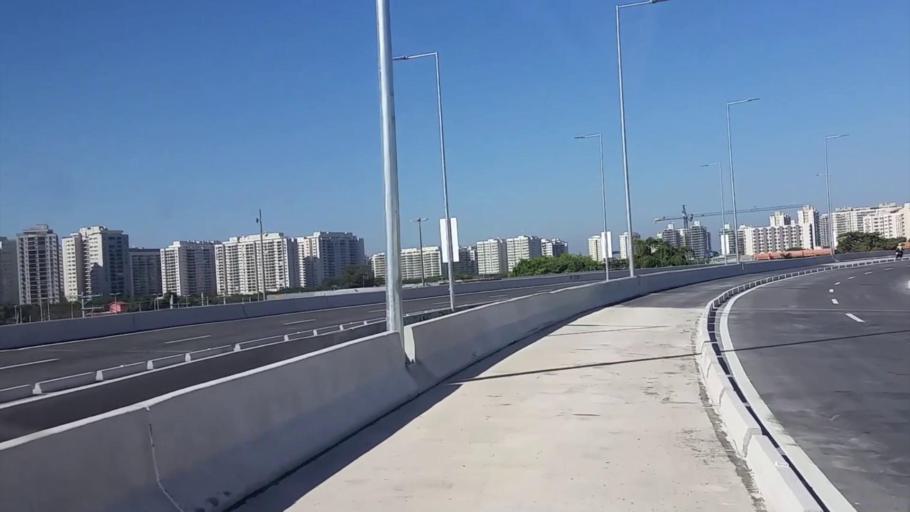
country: BR
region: Rio de Janeiro
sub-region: Nilopolis
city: Nilopolis
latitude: -22.9517
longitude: -43.3899
